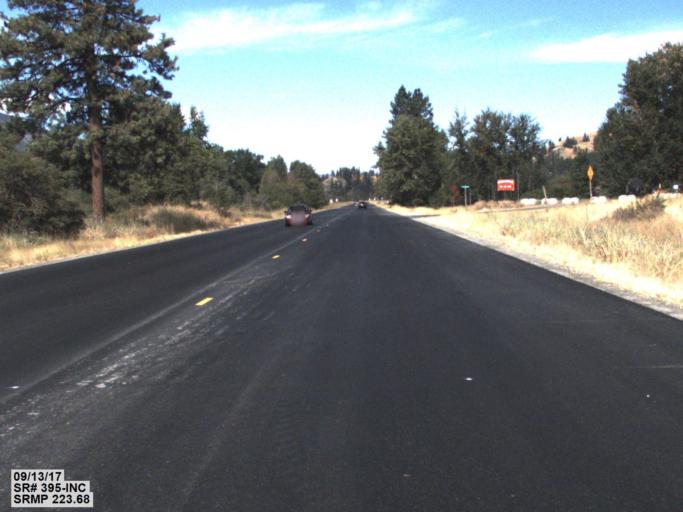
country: US
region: Washington
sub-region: Stevens County
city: Colville
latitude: 48.4641
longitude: -117.8850
